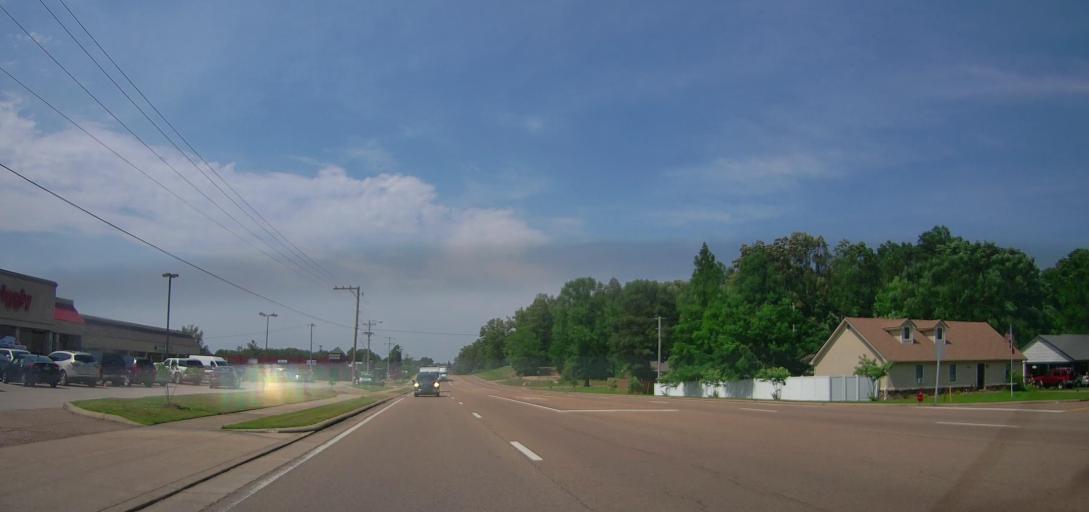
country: US
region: Mississippi
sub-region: De Soto County
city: Olive Branch
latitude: 34.9541
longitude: -89.8305
